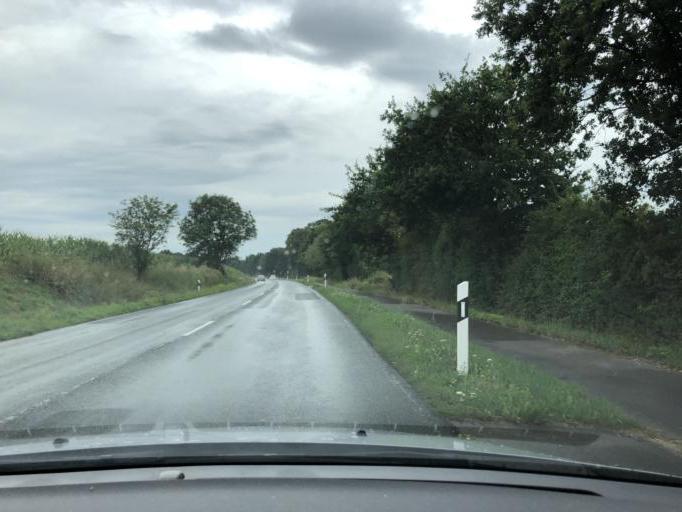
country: DE
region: North Rhine-Westphalia
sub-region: Regierungsbezirk Dusseldorf
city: Schermbeck
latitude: 51.7091
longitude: 6.8739
